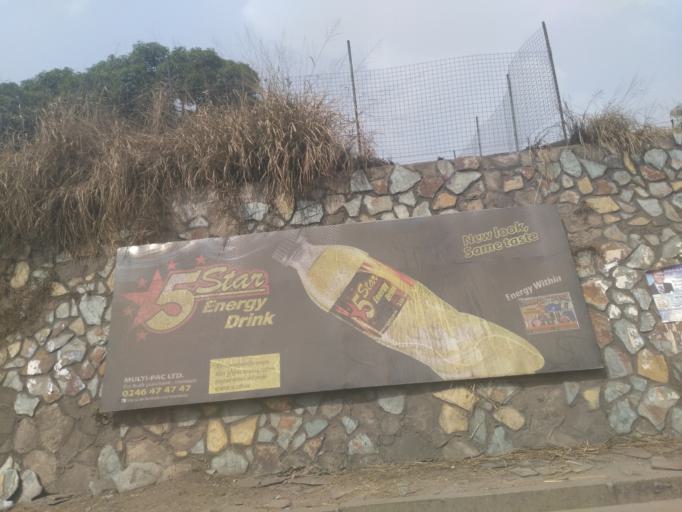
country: GH
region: Ashanti
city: Kumasi
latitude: 6.6872
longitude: -1.5763
